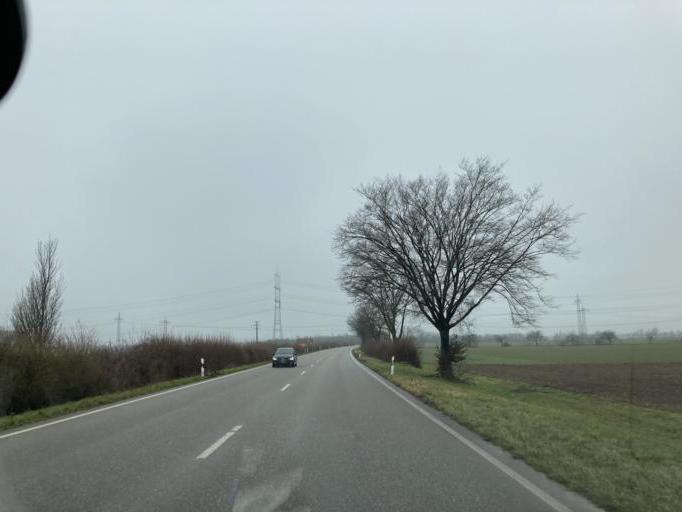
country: DE
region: Baden-Wuerttemberg
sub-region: Freiburg Region
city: Auggen
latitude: 47.8149
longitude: 7.5963
